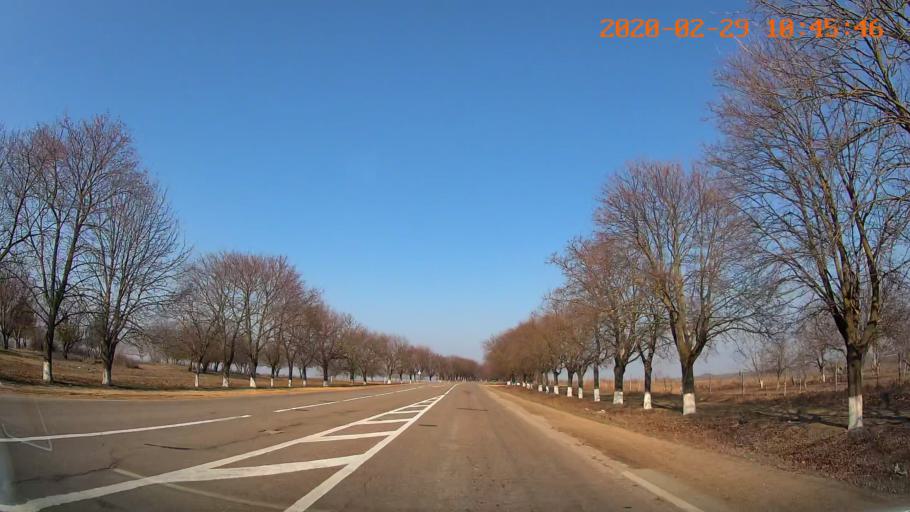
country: MD
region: Telenesti
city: Grigoriopol
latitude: 47.0786
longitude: 29.3796
